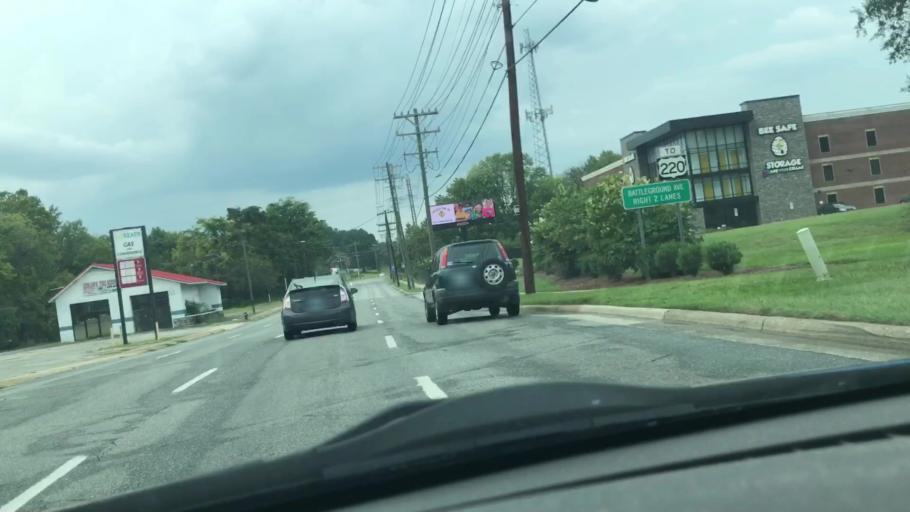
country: US
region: North Carolina
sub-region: Guilford County
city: Greensboro
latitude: 36.0806
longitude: -79.8003
